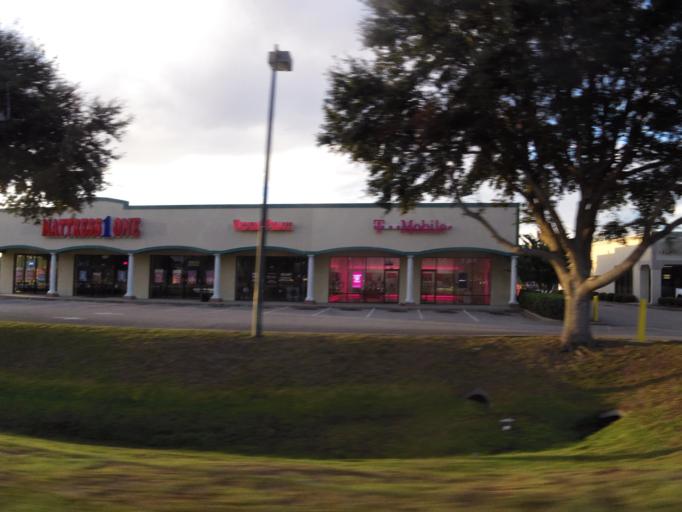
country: US
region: Georgia
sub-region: Glynn County
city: Country Club Estates
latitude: 31.2149
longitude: -81.4858
